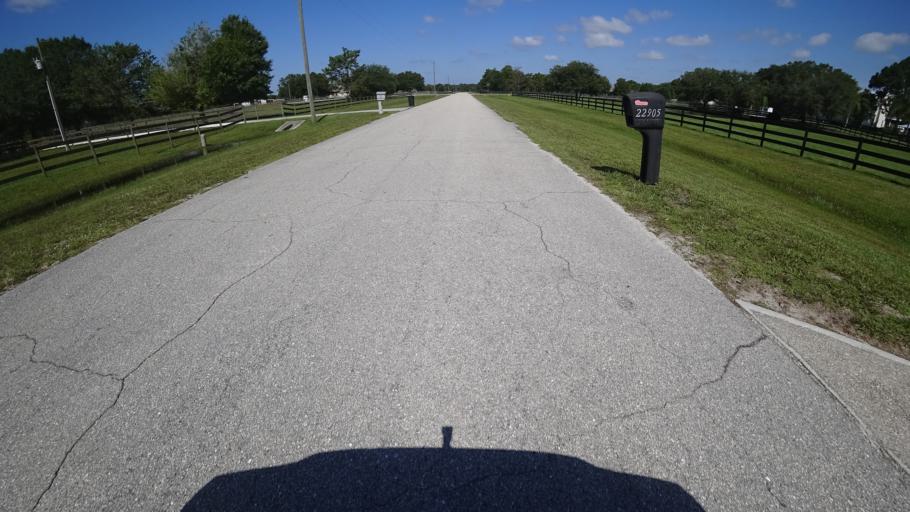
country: US
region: Florida
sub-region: Sarasota County
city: The Meadows
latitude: 27.4201
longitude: -82.3065
